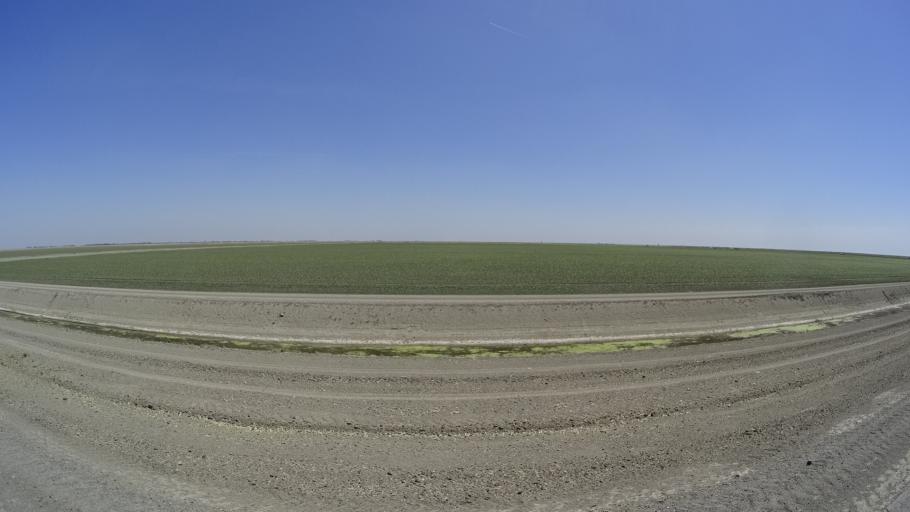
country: US
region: California
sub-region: Kings County
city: Corcoran
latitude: 36.0567
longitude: -119.6435
